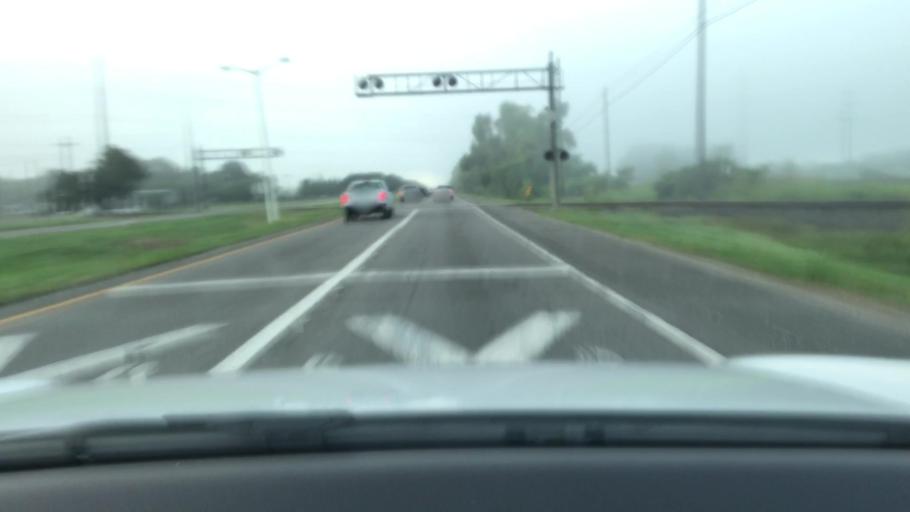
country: US
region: Louisiana
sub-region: West Baton Rouge Parish
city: Addis
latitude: 30.3335
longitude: -91.2576
